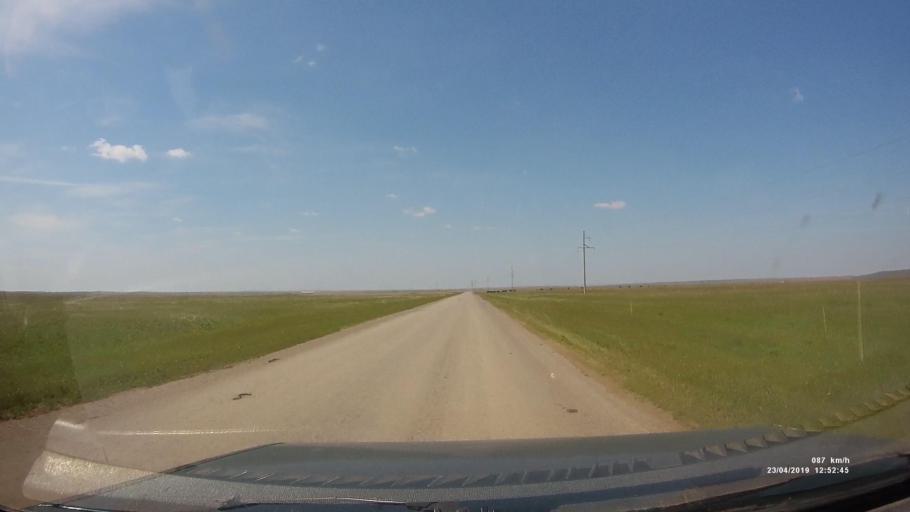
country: RU
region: Kalmykiya
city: Yashalta
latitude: 46.5677
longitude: 42.6054
